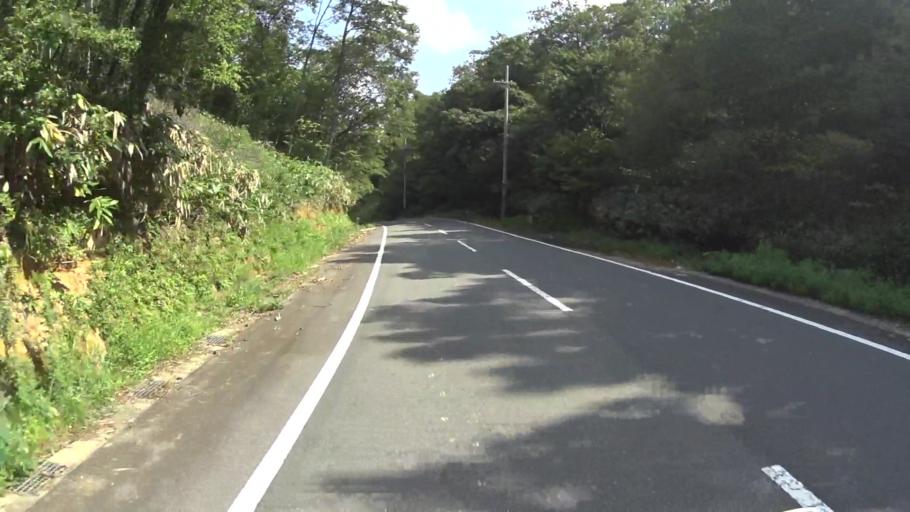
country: JP
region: Kyoto
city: Miyazu
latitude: 35.6267
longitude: 135.2251
